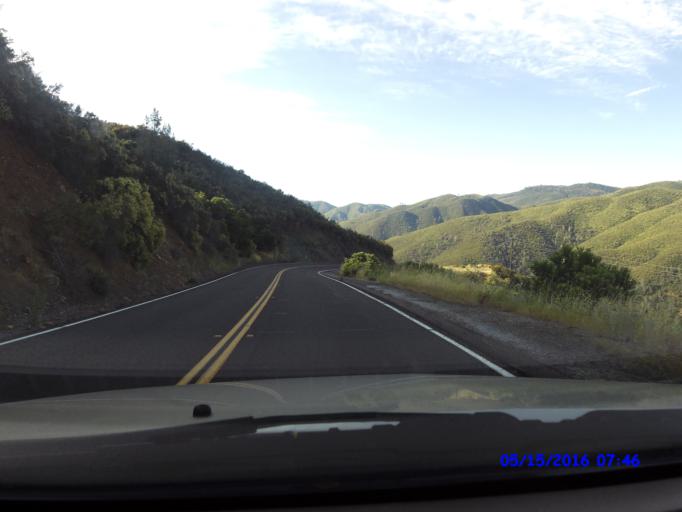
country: US
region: California
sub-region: Mariposa County
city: Mariposa
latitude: 37.6301
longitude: -120.1522
